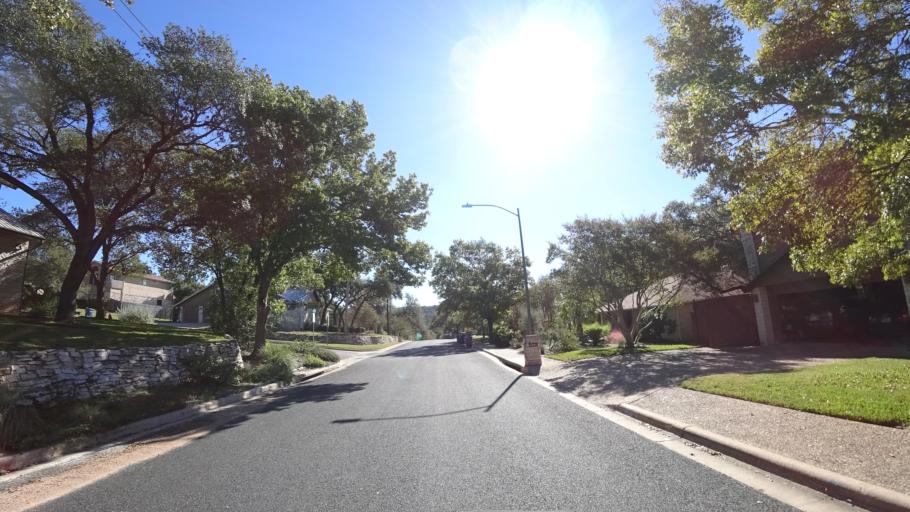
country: US
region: Texas
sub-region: Travis County
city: West Lake Hills
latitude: 30.3605
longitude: -97.7837
